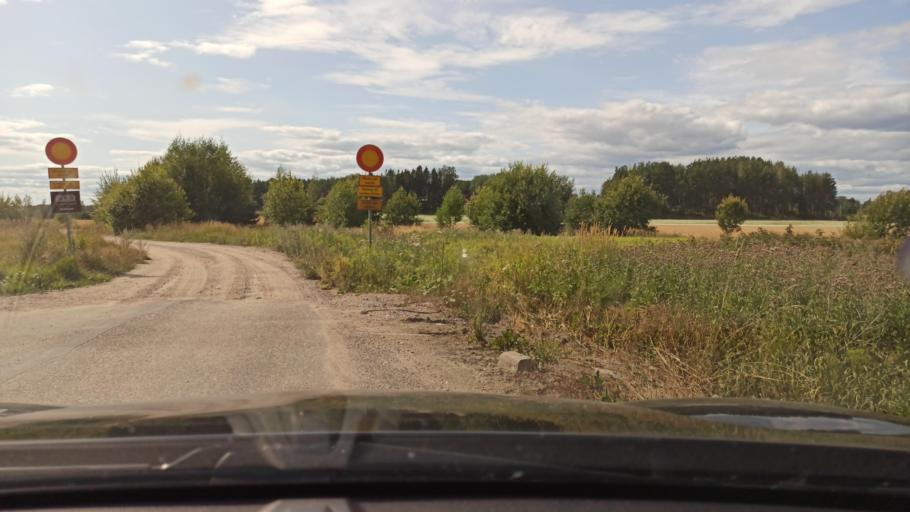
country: FI
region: Uusimaa
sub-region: Helsinki
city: Kirkkonummi
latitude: 60.1172
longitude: 24.4211
